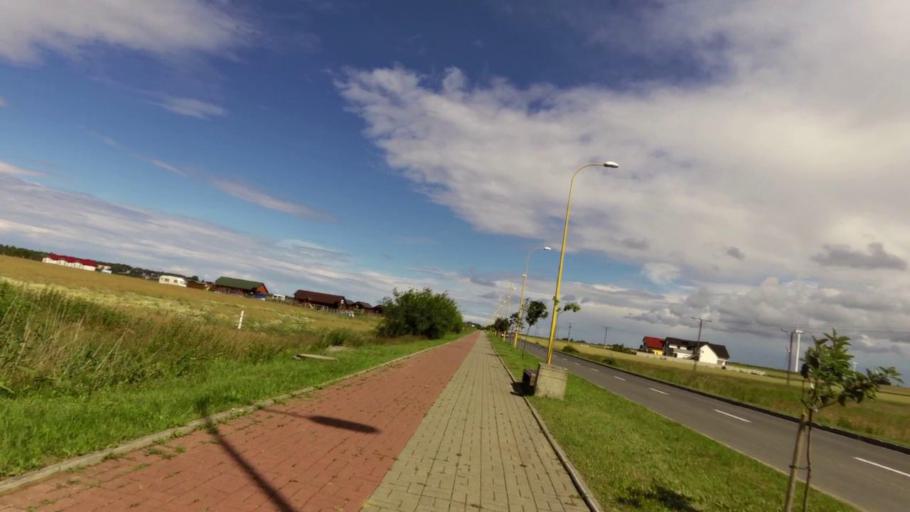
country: PL
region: West Pomeranian Voivodeship
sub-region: Powiat slawienski
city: Darlowo
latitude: 54.4357
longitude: 16.4101
